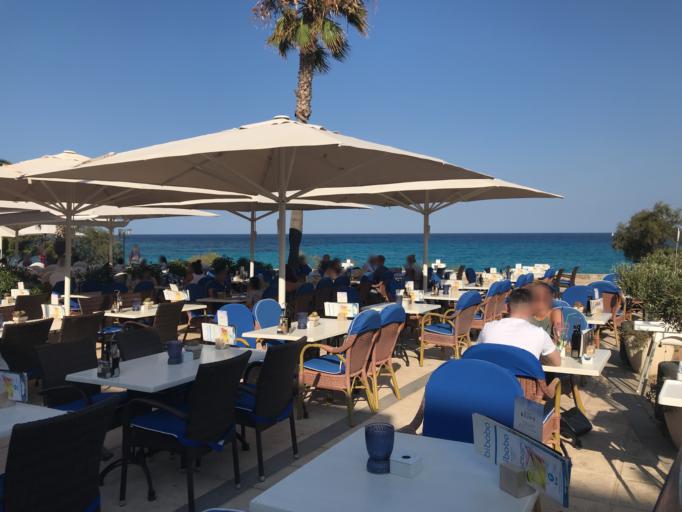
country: ES
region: Balearic Islands
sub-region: Illes Balears
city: Son Servera
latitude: 39.5678
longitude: 3.3733
